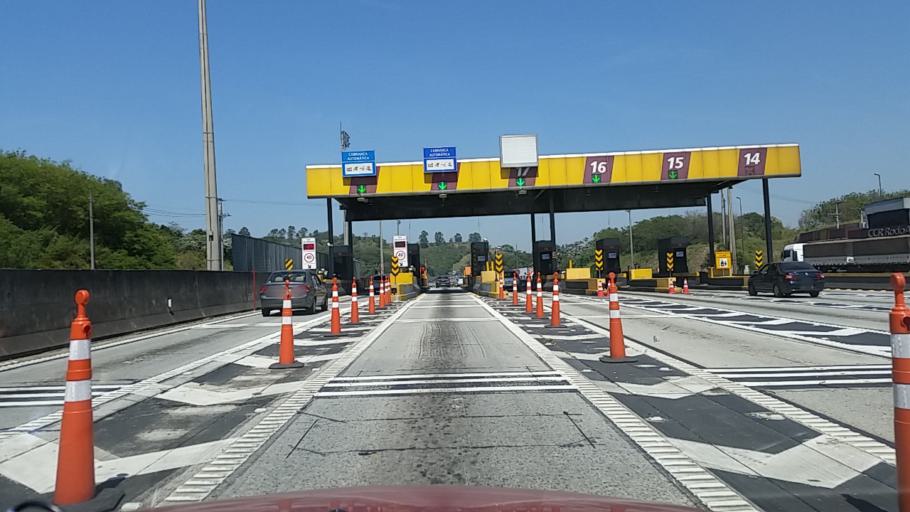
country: BR
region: Sao Paulo
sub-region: Taboao Da Serra
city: Taboao da Serra
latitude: -23.6016
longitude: -46.8129
